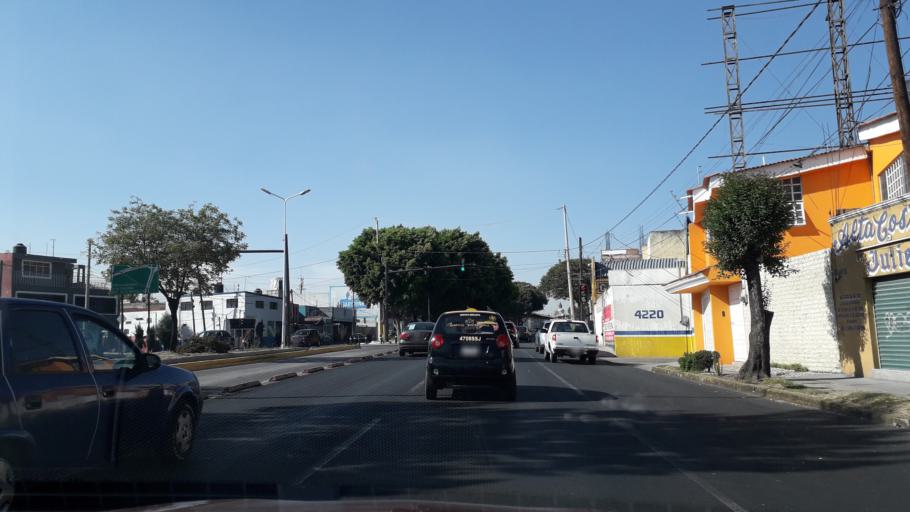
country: MX
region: Puebla
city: Puebla
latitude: 19.0621
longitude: -98.1919
